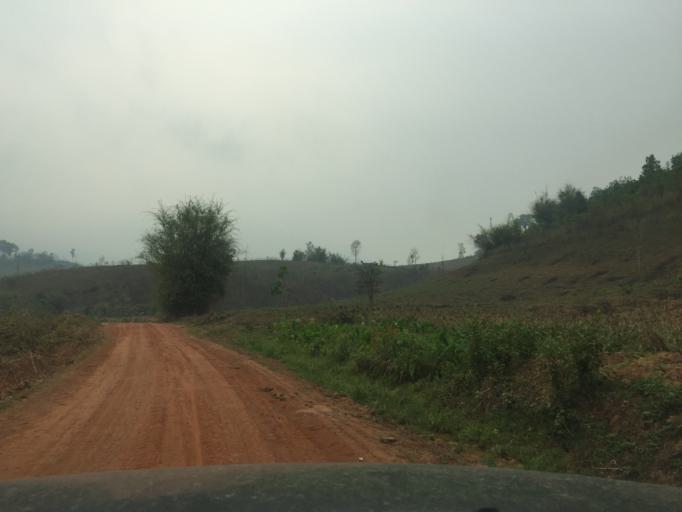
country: TH
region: Nan
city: Bo Kluea
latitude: 18.8522
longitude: 101.4172
